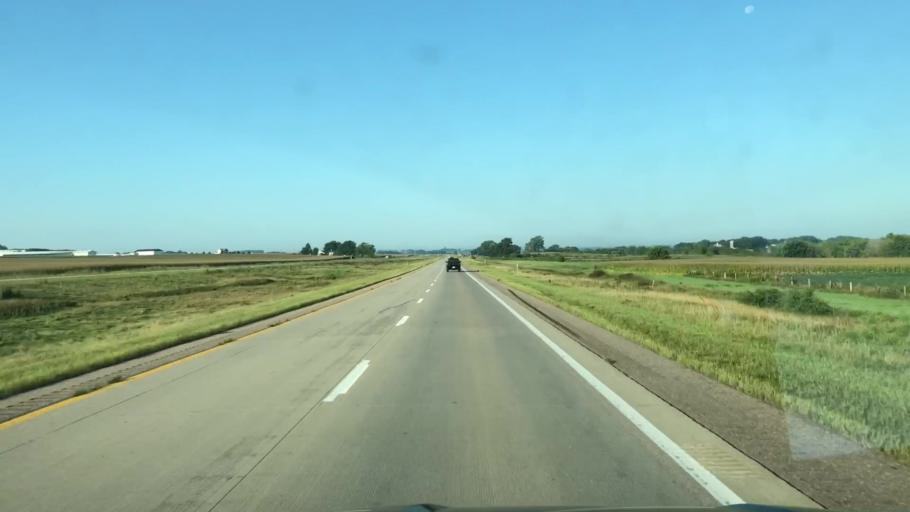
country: US
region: Iowa
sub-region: Sioux County
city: Alton
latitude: 43.0309
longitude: -95.9324
